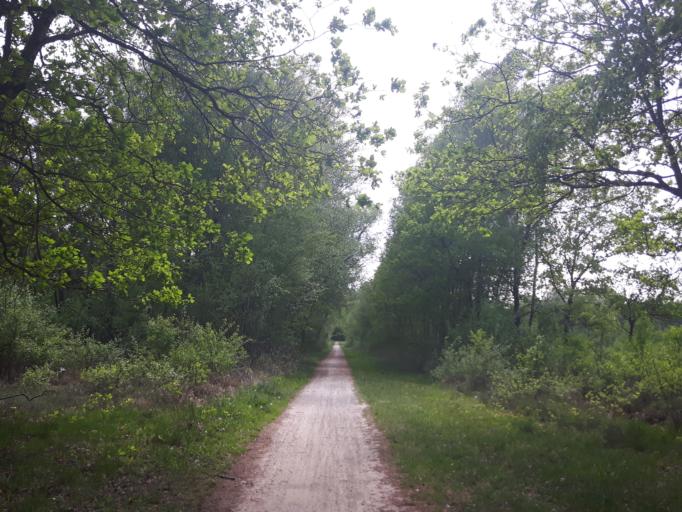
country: NL
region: Overijssel
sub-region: Gemeente Enschede
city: Enschede
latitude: 52.1485
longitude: 6.8710
